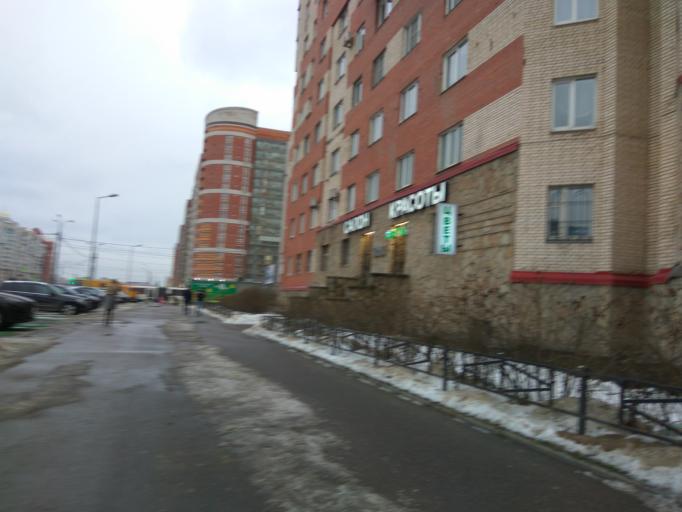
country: RU
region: St.-Petersburg
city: Staraya Derevnya
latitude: 60.0022
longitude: 30.2433
